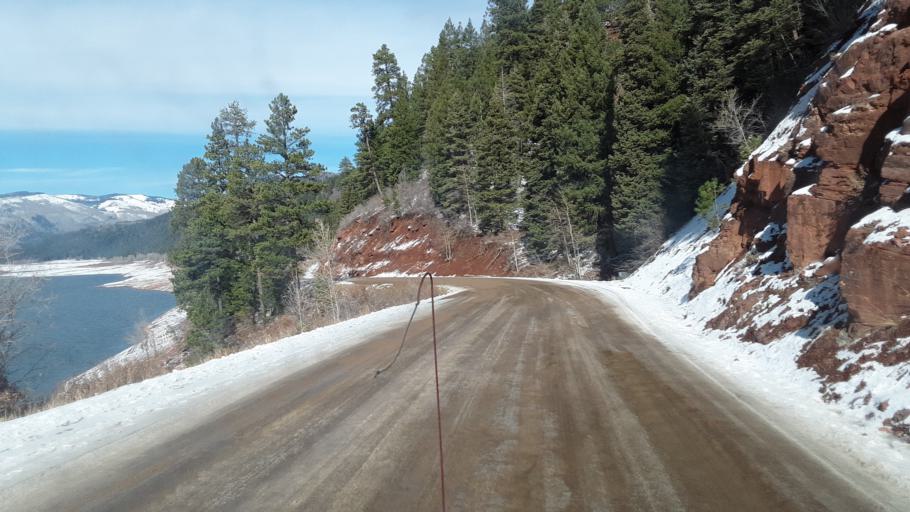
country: US
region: Colorado
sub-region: La Plata County
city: Bayfield
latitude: 37.3866
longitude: -107.6568
